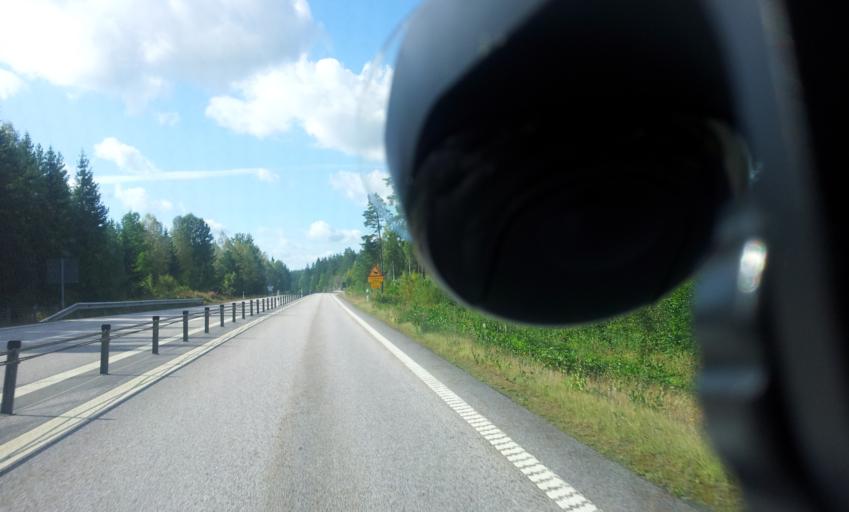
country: SE
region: Kalmar
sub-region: Vasterviks Kommun
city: Forserum
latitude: 58.0410
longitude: 16.5216
